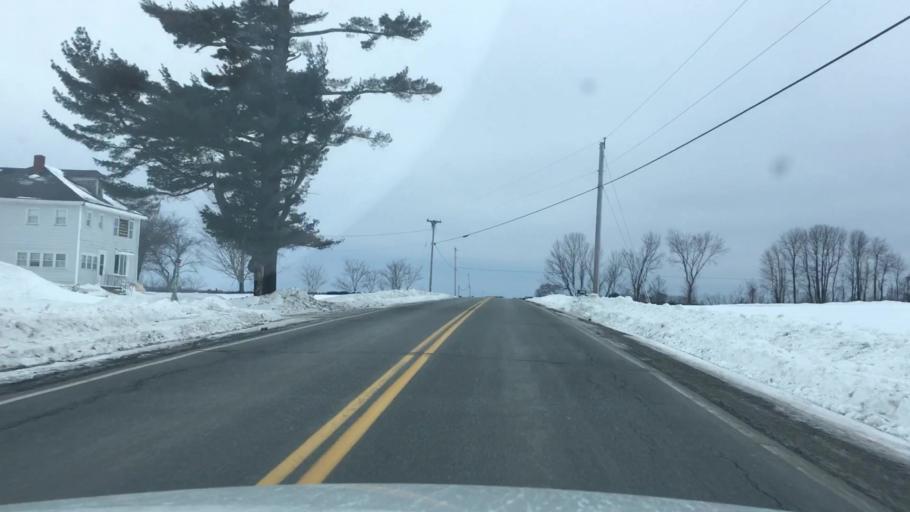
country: US
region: Maine
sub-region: Penobscot County
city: Garland
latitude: 44.9667
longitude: -69.1664
